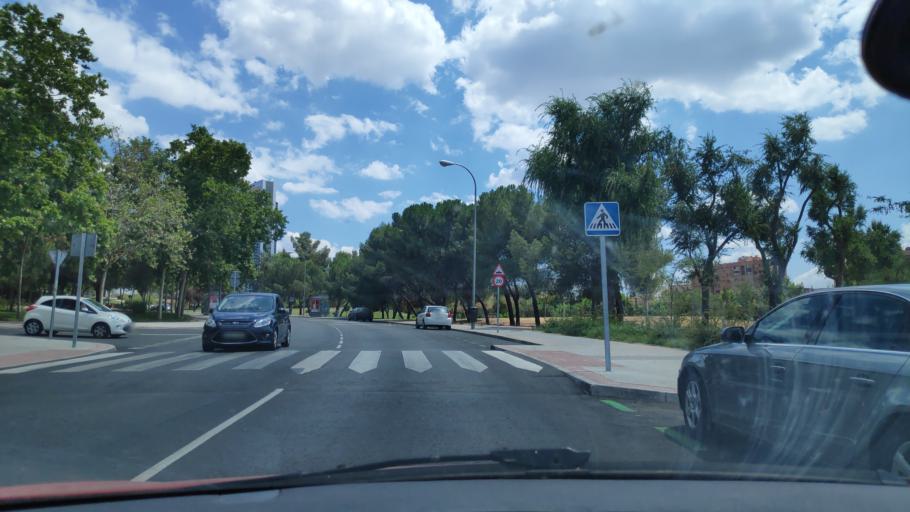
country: ES
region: Madrid
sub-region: Provincia de Madrid
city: Tetuan de las Victorias
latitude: 40.4819
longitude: -3.6979
